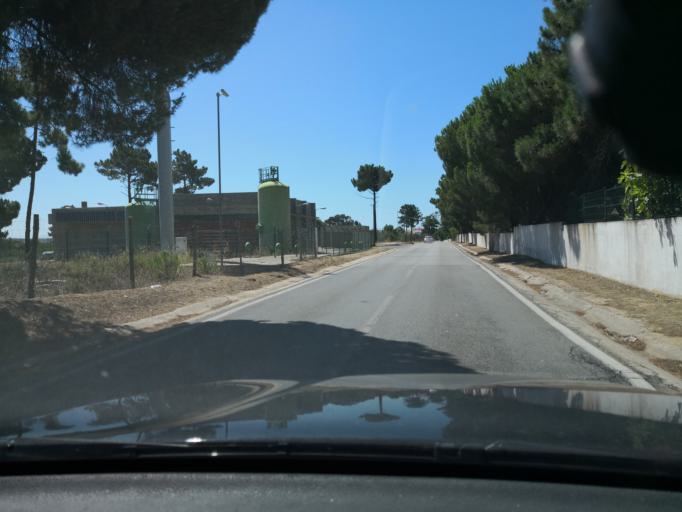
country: PT
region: Faro
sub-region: Loule
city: Vilamoura
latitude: 37.0815
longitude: -8.0995
